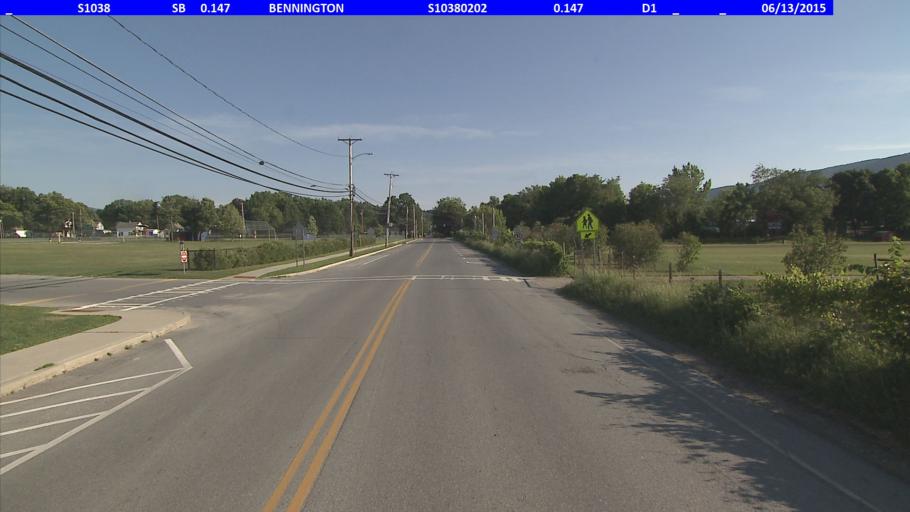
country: US
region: Vermont
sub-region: Bennington County
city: Bennington
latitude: 42.8864
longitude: -73.1929
